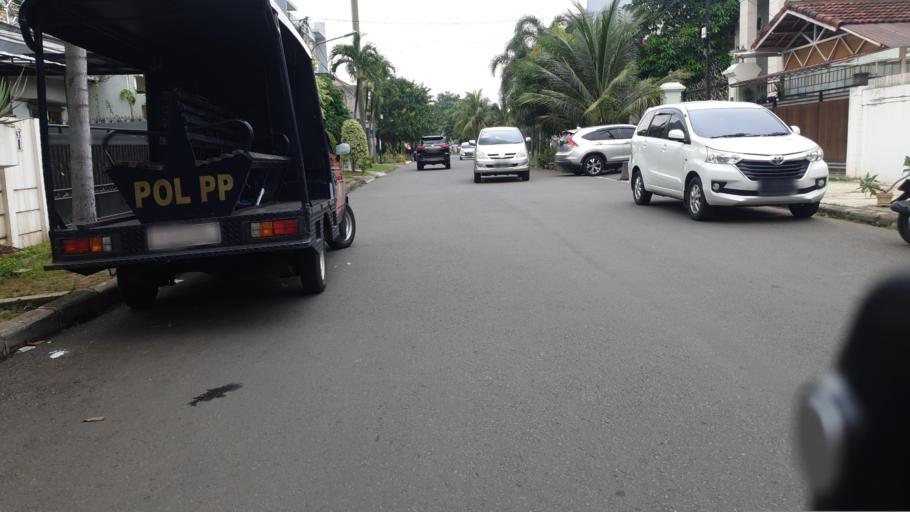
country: ID
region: West Java
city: Ciputat
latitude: -6.1921
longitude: 106.7507
